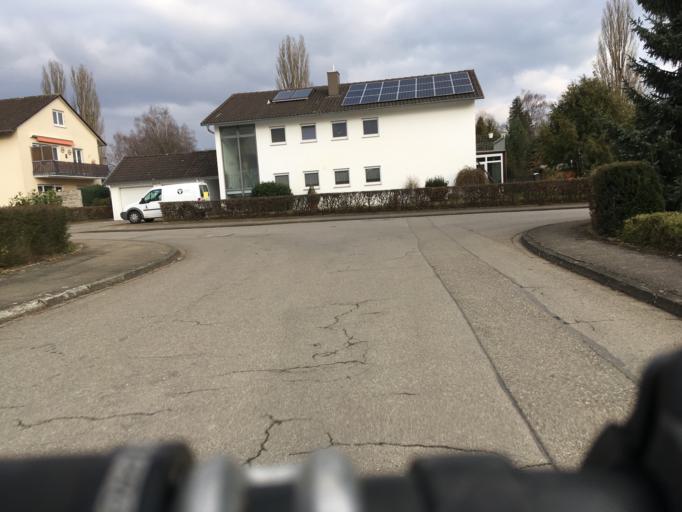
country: DE
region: Baden-Wuerttemberg
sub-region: Freiburg Region
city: Gottmadingen
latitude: 47.7283
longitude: 8.7748
